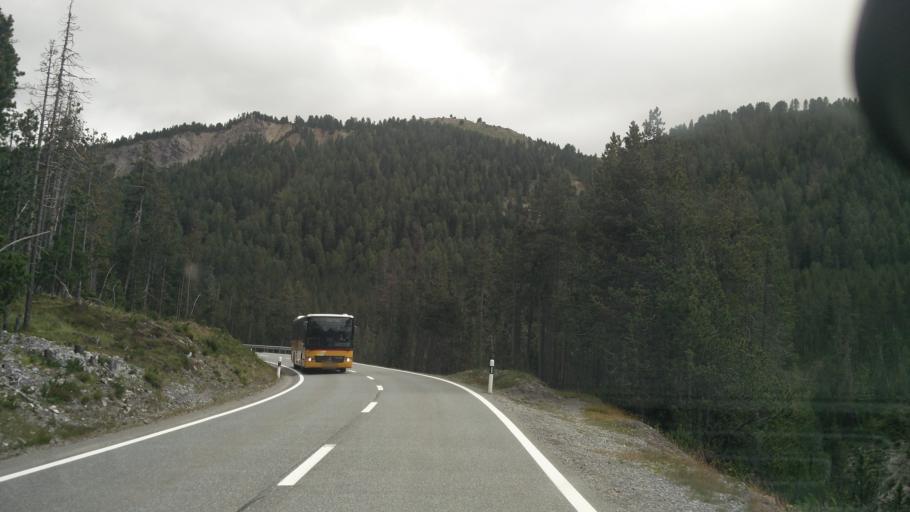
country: CH
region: Grisons
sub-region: Inn District
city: Scuol
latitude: 46.6551
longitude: 10.2490
